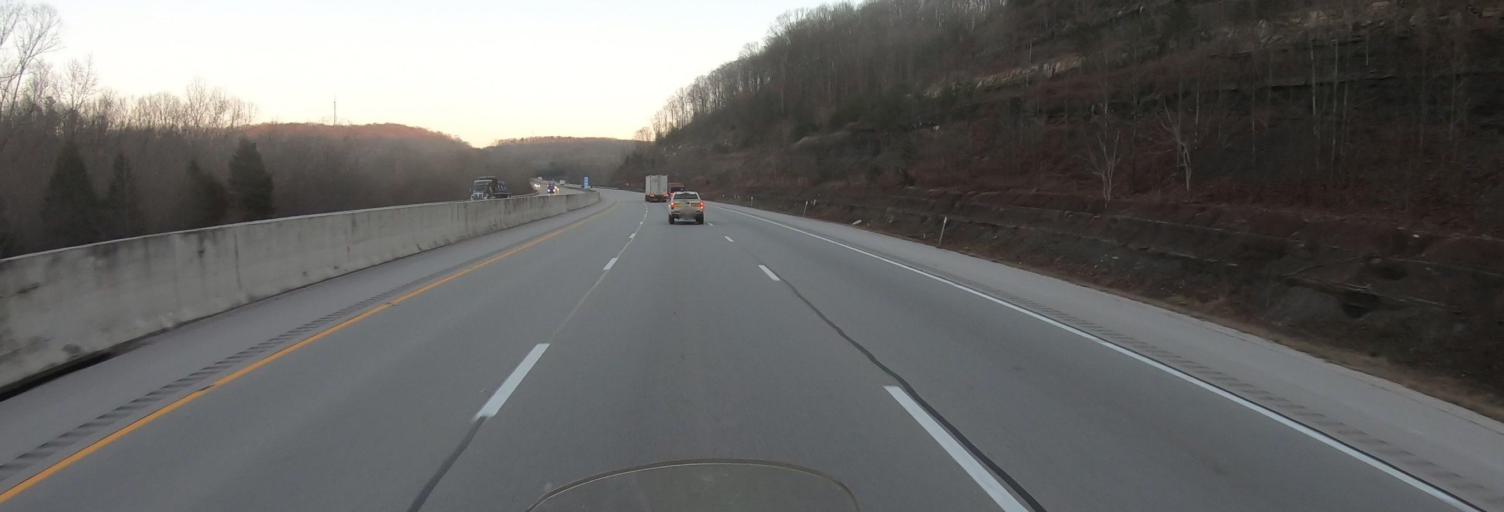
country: US
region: Kentucky
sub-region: Rockcastle County
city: Mount Vernon
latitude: 37.2469
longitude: -84.2404
